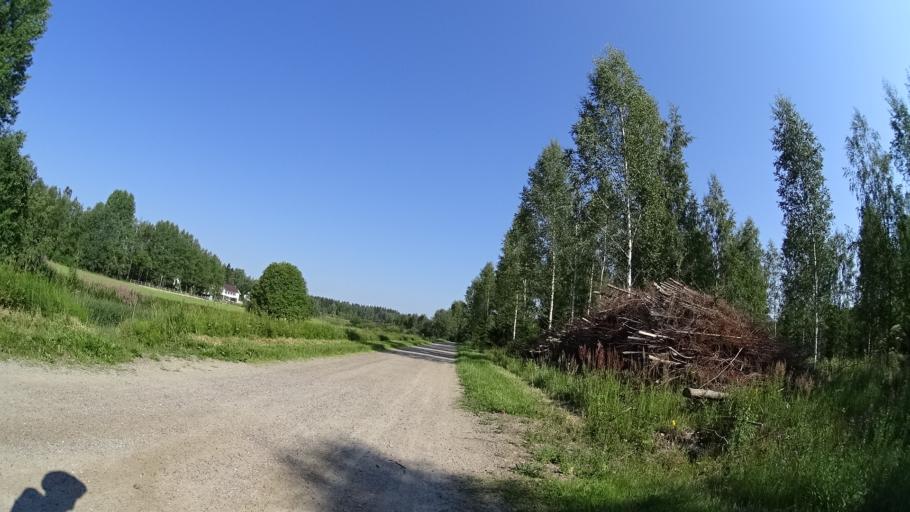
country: FI
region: Uusimaa
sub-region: Helsinki
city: Kerava
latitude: 60.3576
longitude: 25.1250
